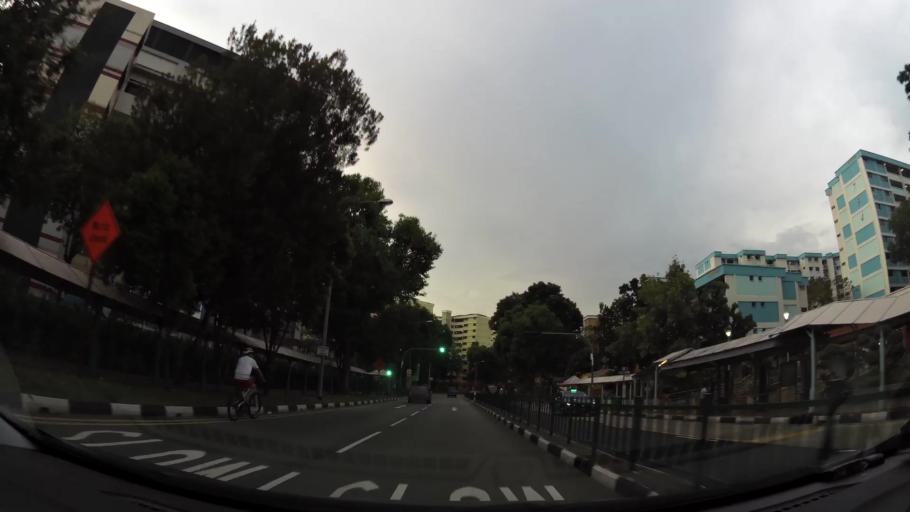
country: MY
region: Johor
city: Kampung Pasir Gudang Baru
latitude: 1.4285
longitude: 103.8306
